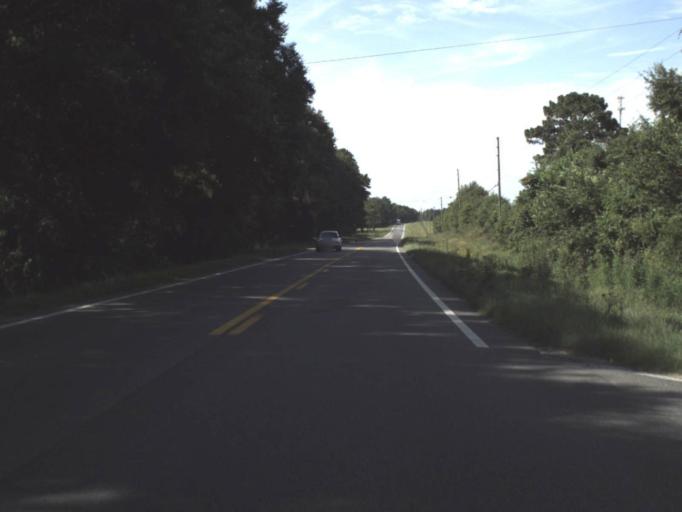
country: US
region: Florida
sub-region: Madison County
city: Madison
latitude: 30.5298
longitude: -83.3676
